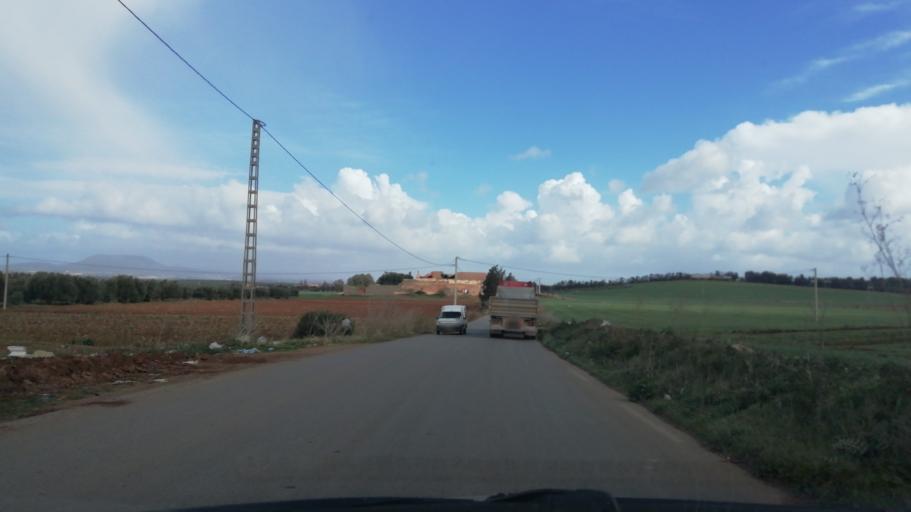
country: DZ
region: Oran
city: Sidi ech Chahmi
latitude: 35.6396
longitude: -0.5189
